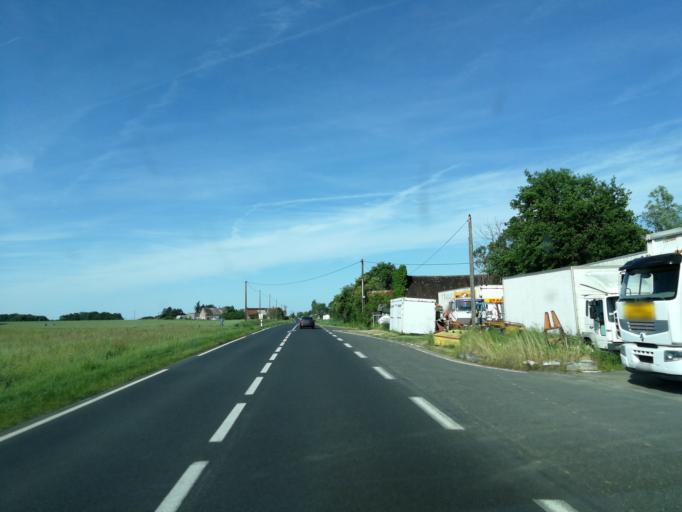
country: FR
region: Centre
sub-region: Departement d'Indre-et-Loire
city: Villedomer
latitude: 47.5300
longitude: 0.8360
